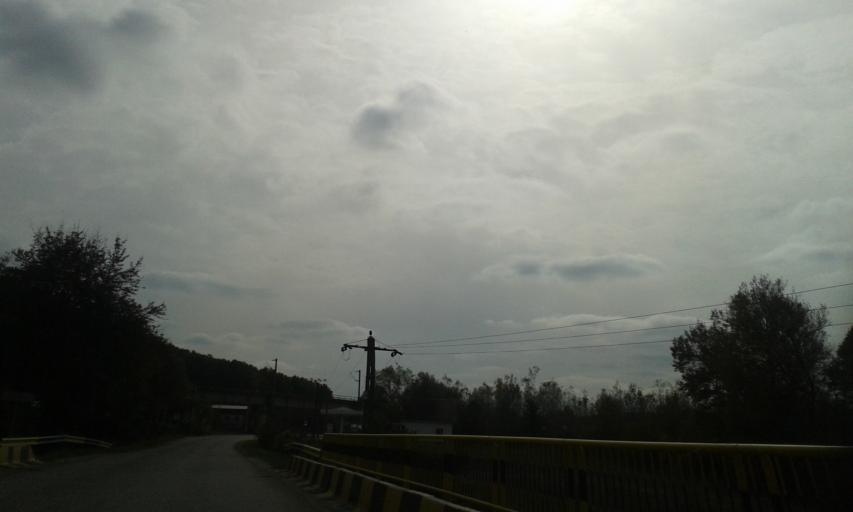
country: RO
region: Gorj
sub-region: Comuna Targu Carbunesti
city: Pojogeni
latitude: 44.9750
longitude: 23.5026
